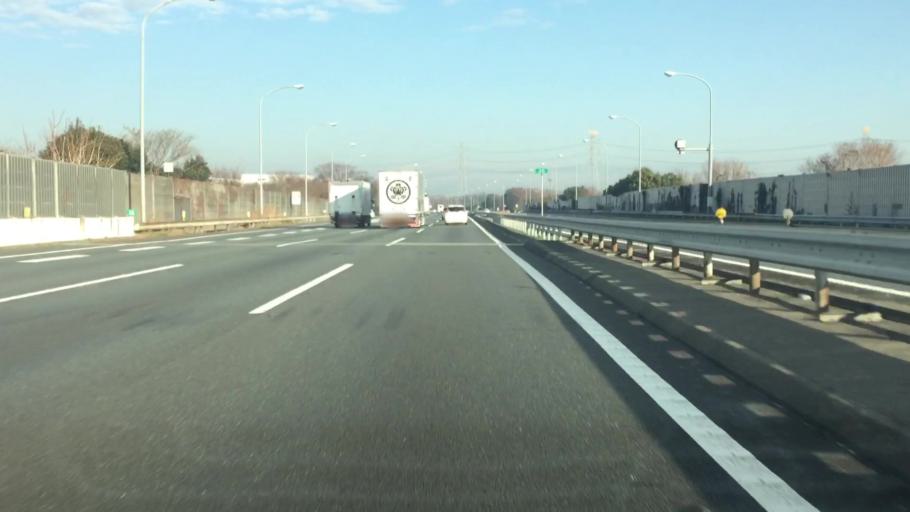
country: JP
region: Saitama
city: Sakado
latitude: 36.0229
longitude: 139.3821
